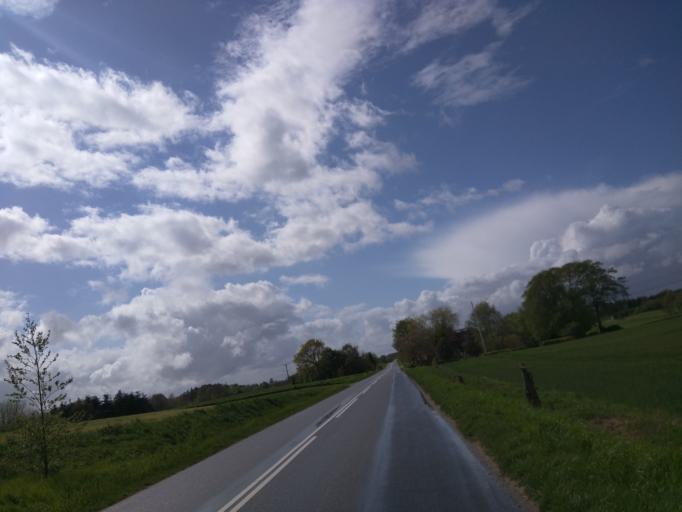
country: DK
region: Central Jutland
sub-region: Silkeborg Kommune
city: Kjellerup
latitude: 56.2771
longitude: 9.5039
